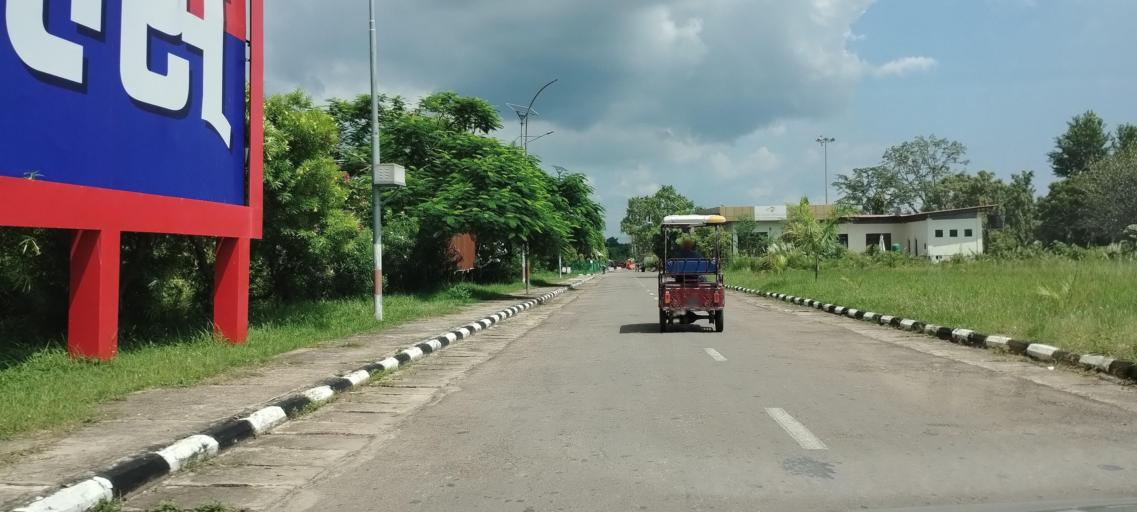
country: NP
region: Mid Western
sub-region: Bheri Zone
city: Nepalgunj
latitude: 28.1006
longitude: 81.6660
